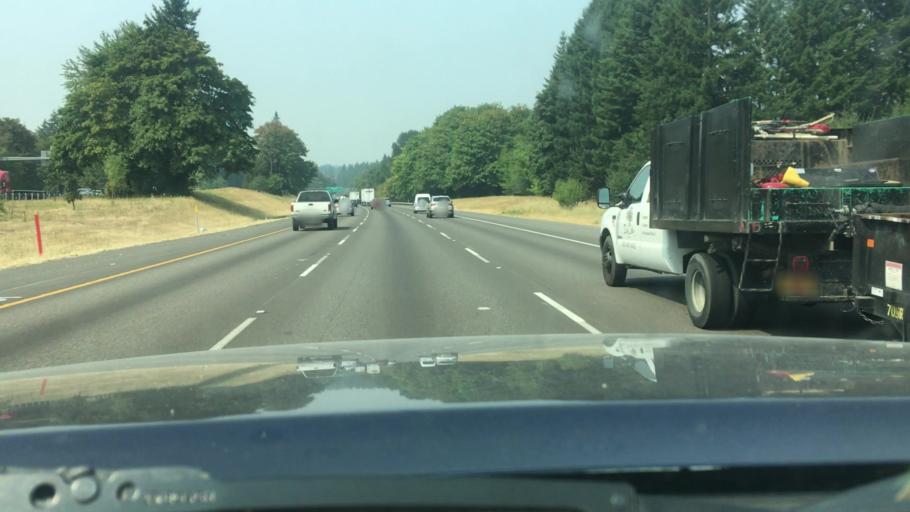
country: US
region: Oregon
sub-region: Clackamas County
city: Stafford
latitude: 45.3734
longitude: -122.7215
